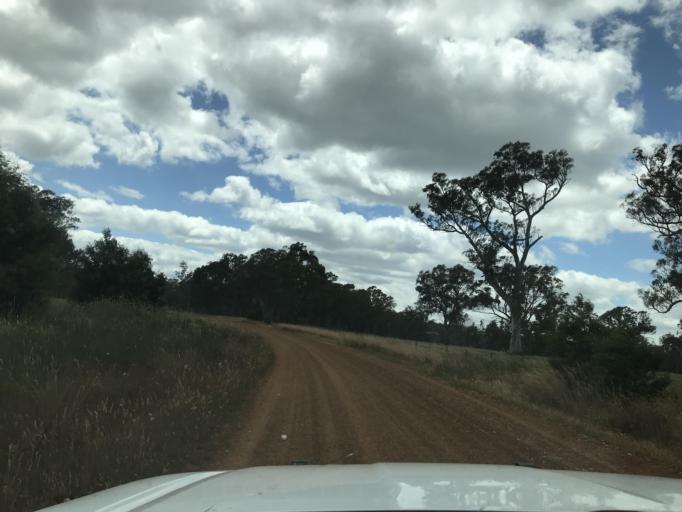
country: AU
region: South Australia
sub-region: Wattle Range
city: Penola
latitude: -37.3719
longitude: 141.2354
